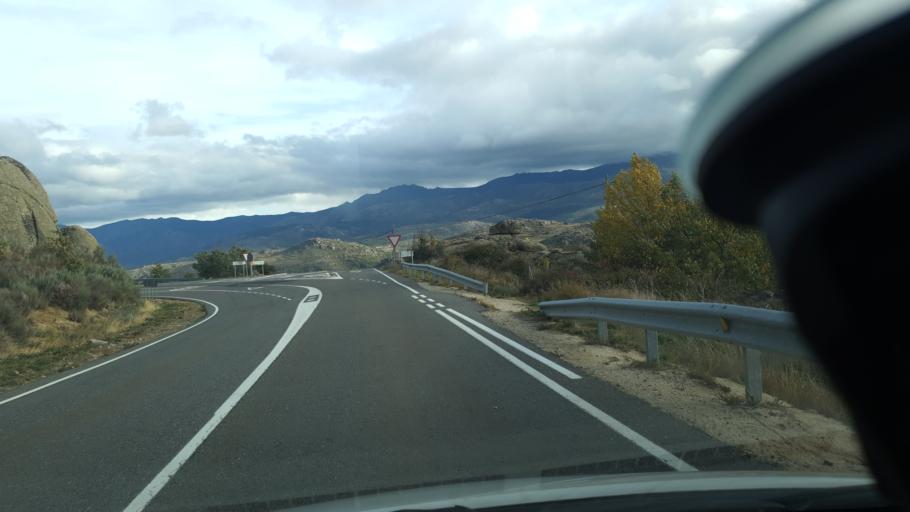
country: ES
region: Castille and Leon
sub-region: Provincia de Avila
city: Navalosa
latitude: 40.3957
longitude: -4.9231
